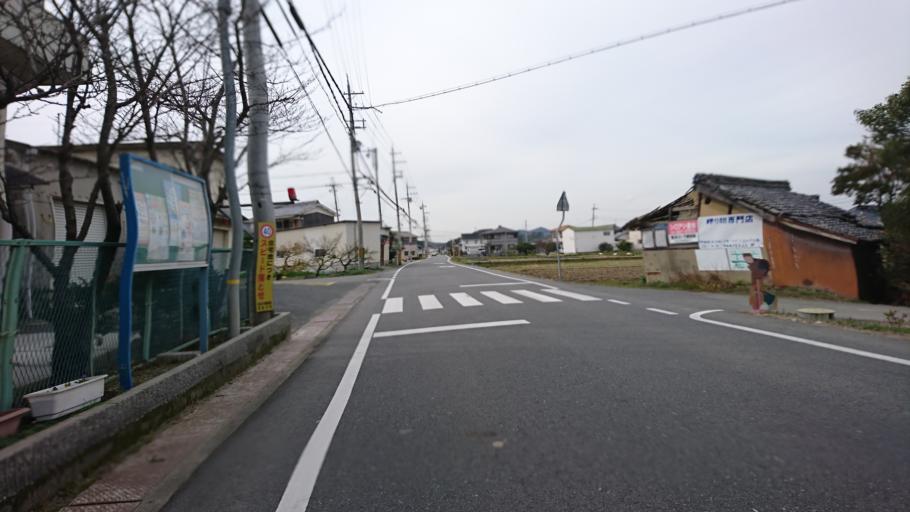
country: JP
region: Hyogo
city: Ono
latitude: 34.7847
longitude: 134.9103
